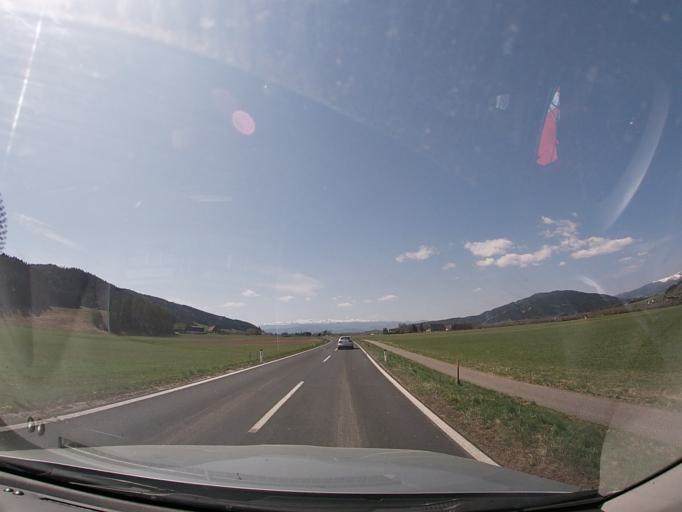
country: AT
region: Styria
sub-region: Politischer Bezirk Murtal
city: Sankt Lorenzen bei Knittelfeld
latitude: 47.2459
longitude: 14.8872
